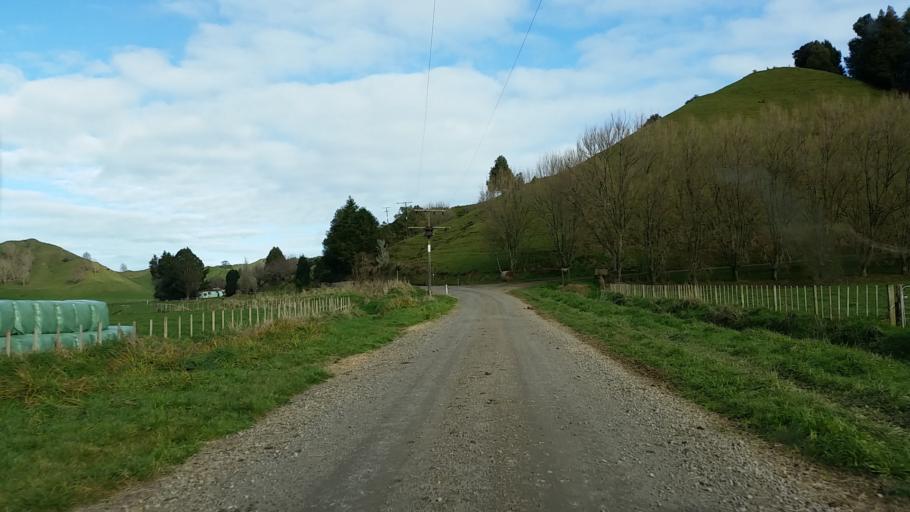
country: NZ
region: Taranaki
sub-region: South Taranaki District
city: Eltham
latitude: -39.2510
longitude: 174.5354
